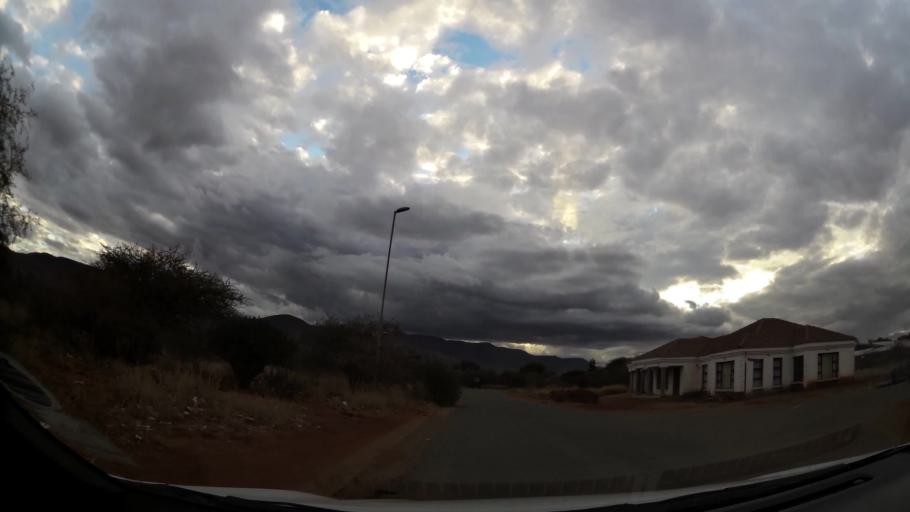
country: ZA
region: Limpopo
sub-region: Waterberg District Municipality
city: Mokopane
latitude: -24.2021
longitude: 28.9936
